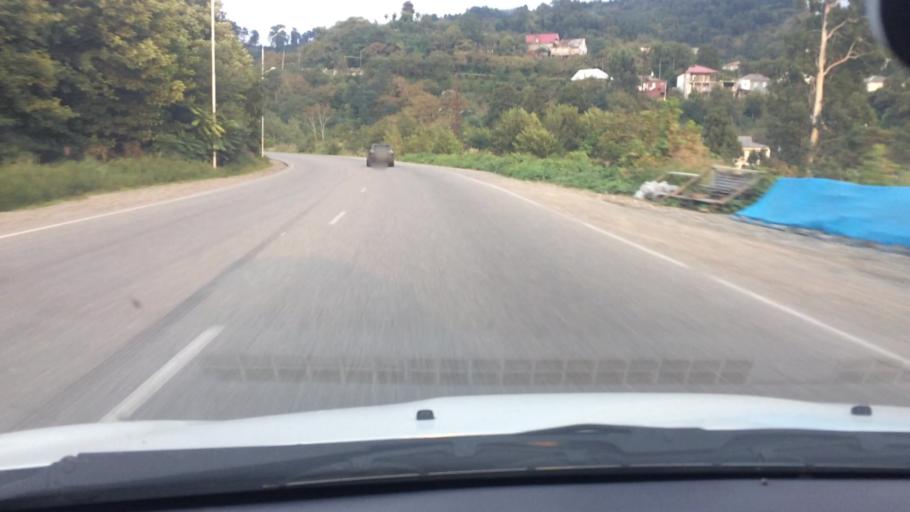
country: GE
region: Ajaria
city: Makhinjauri
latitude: 41.6871
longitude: 41.7076
